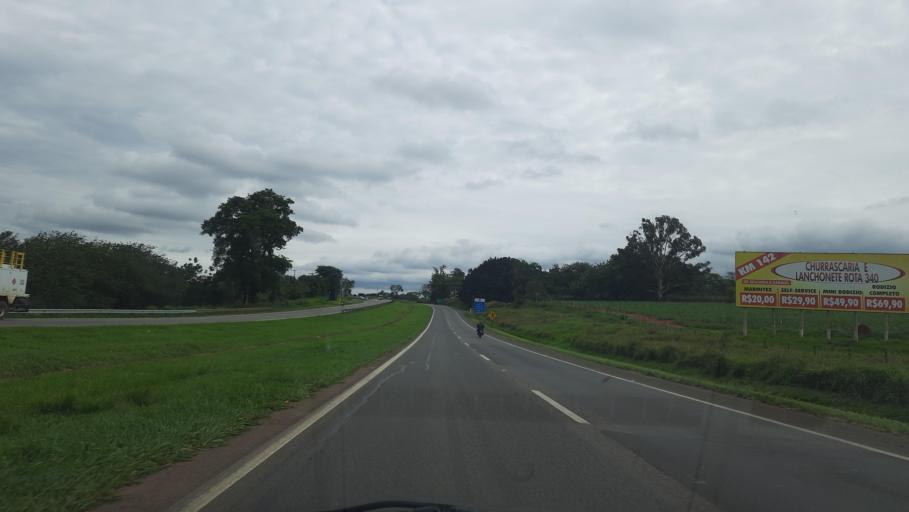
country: BR
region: Sao Paulo
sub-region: Mogi-Mirim
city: Mogi Mirim
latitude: -22.4317
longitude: -46.9843
